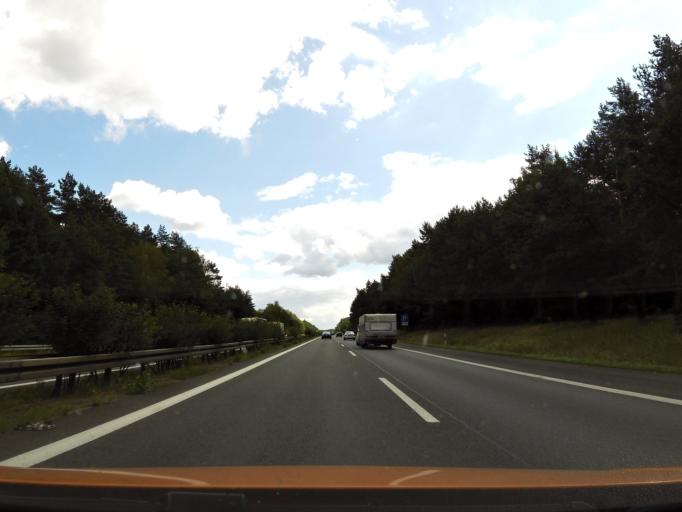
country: DE
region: Brandenburg
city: Birkenwerder
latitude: 52.6923
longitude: 13.3128
